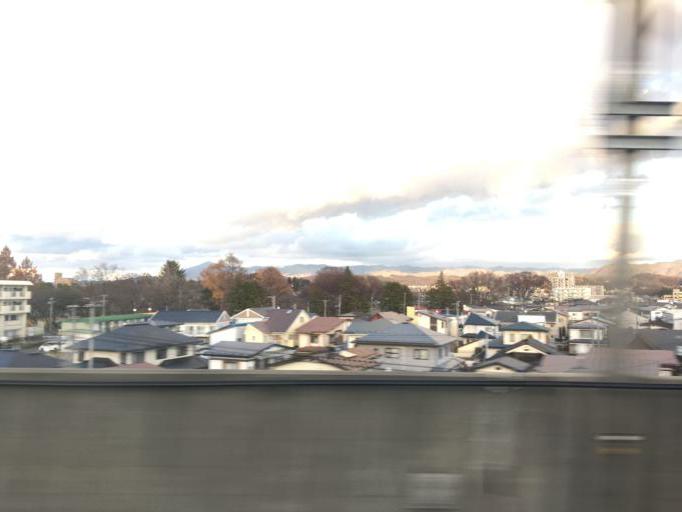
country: JP
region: Iwate
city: Morioka-shi
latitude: 39.7156
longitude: 141.1209
